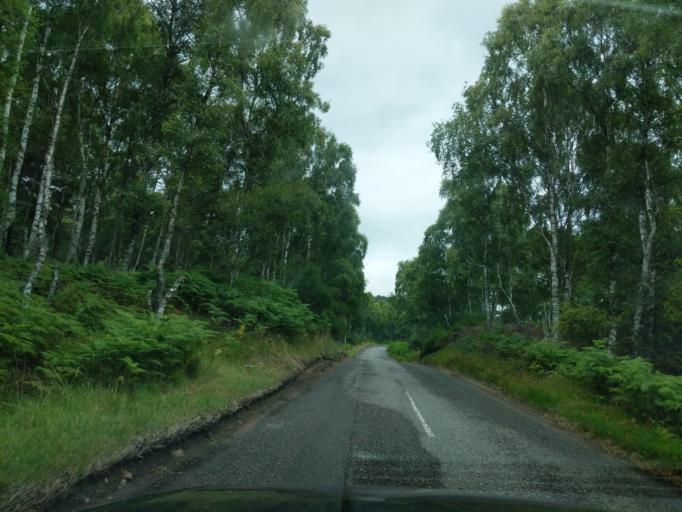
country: GB
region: Scotland
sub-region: Aberdeenshire
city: Ballater
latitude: 57.0689
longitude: -2.9476
